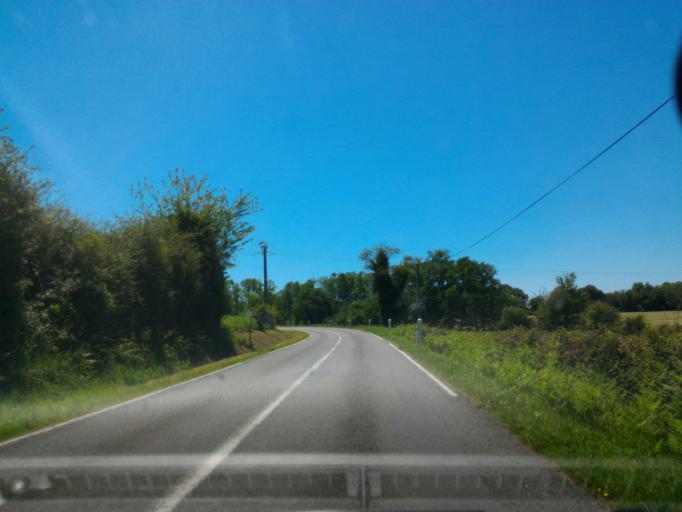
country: FR
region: Poitou-Charentes
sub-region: Departement de la Vienne
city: Availles-Limouzine
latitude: 46.1869
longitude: 0.7259
